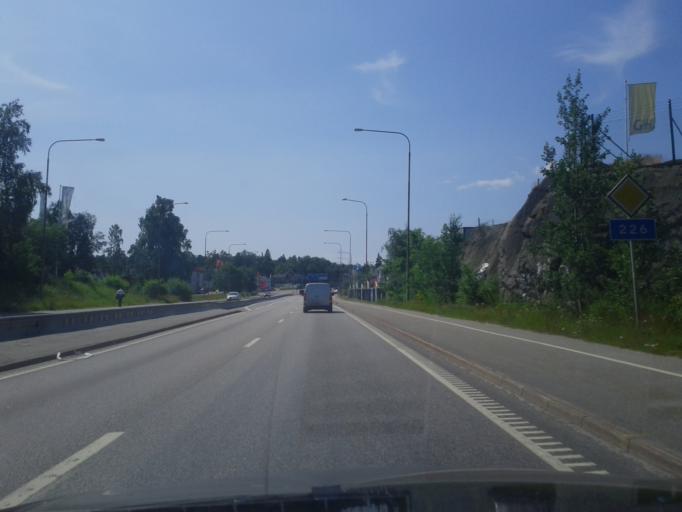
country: SE
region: Stockholm
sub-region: Huddinge Kommun
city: Huddinge
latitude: 59.2531
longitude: 18.0114
